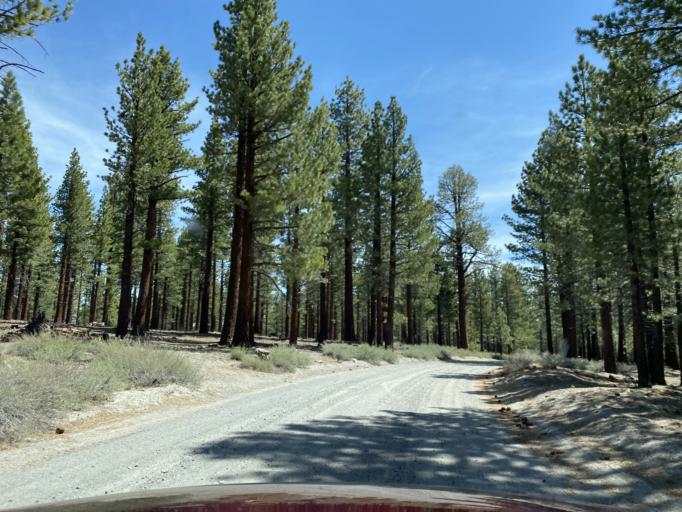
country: US
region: California
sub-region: Mono County
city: Mammoth Lakes
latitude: 37.7692
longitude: -119.0213
